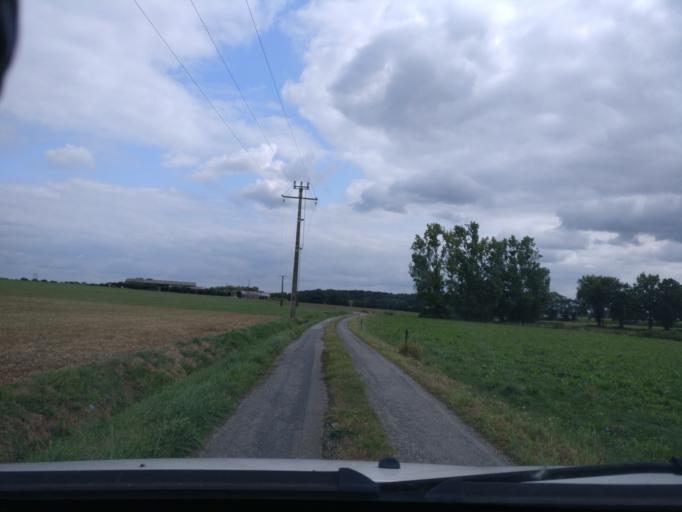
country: FR
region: Brittany
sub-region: Departement d'Ille-et-Vilaine
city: Nouvoitou
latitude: 48.0706
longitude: -1.5602
